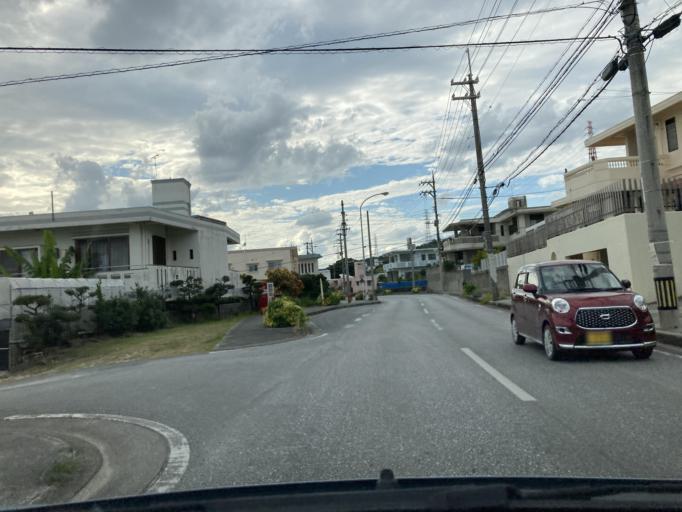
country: JP
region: Okinawa
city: Gushikawa
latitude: 26.3489
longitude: 127.8550
